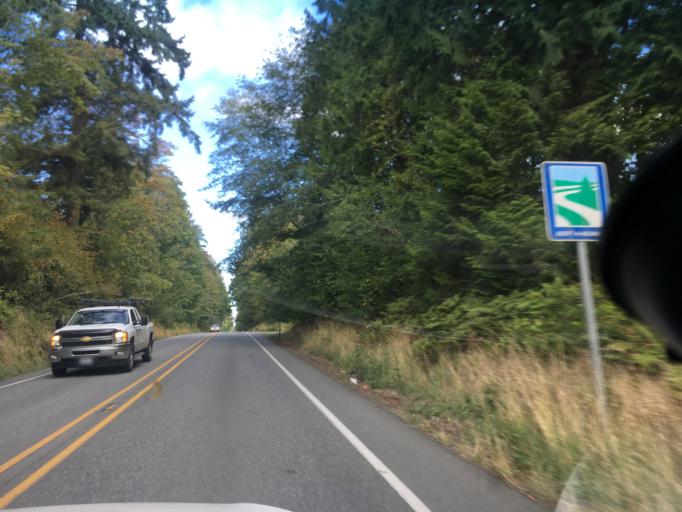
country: US
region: Washington
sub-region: Kitsap County
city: Lofall
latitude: 47.8430
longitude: -122.5867
